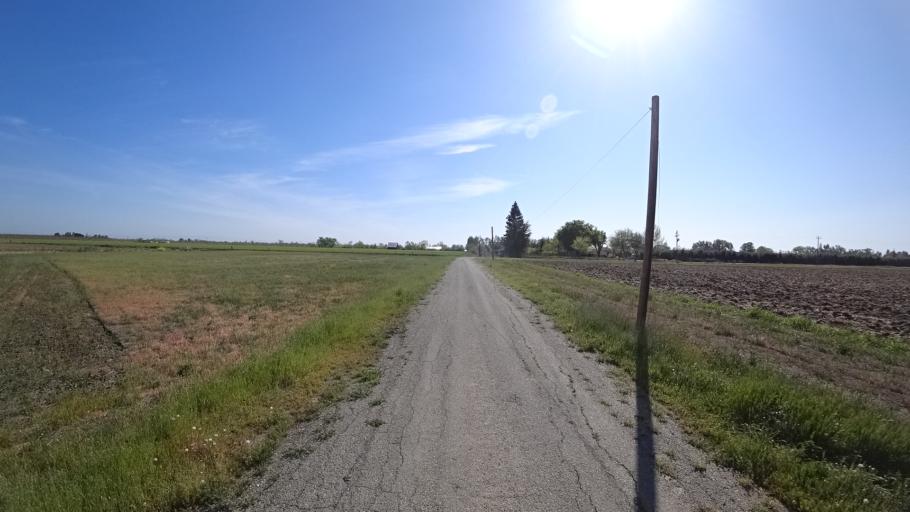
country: US
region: California
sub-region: Glenn County
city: Willows
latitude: 39.5461
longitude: -122.1710
